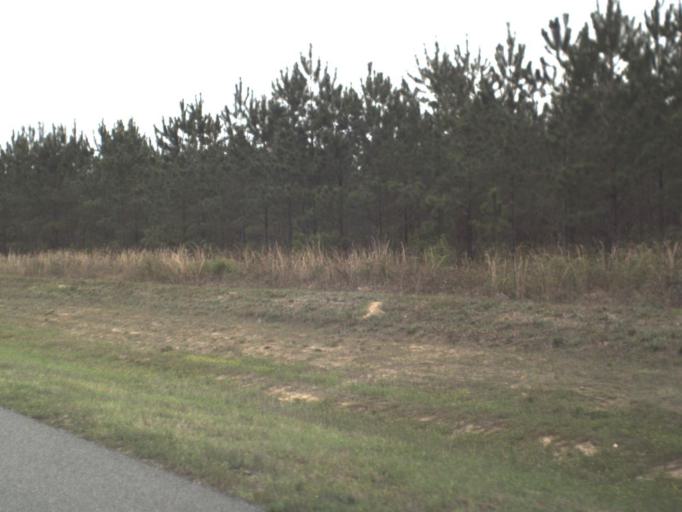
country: US
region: Florida
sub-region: Gulf County
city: Wewahitchka
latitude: 30.3214
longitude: -85.2292
